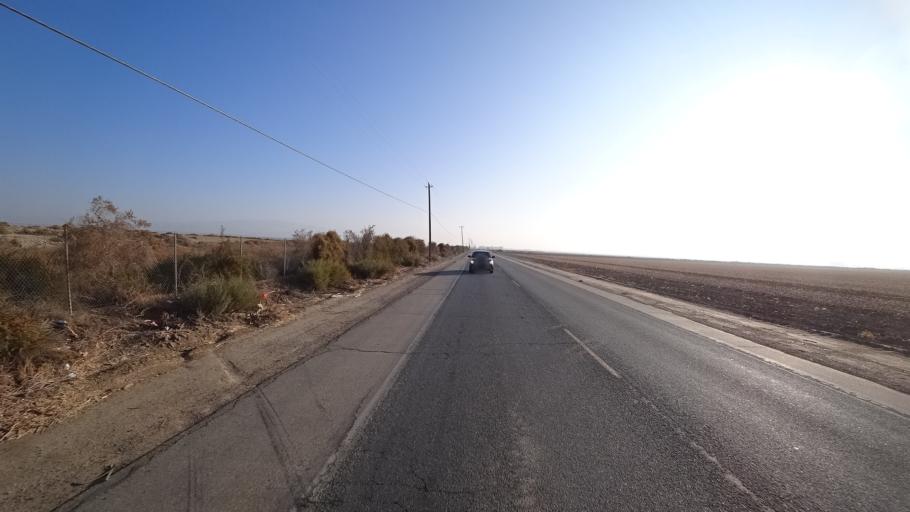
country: US
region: California
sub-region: Kern County
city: Greenfield
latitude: 35.2669
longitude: -118.9708
